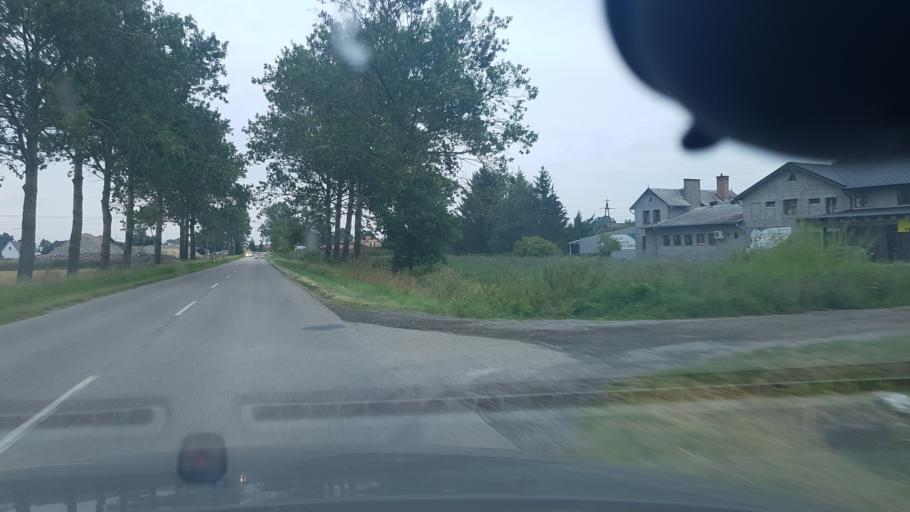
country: PL
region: Pomeranian Voivodeship
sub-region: Powiat nowodworski
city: Nowy Dwor Gdanski
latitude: 54.2180
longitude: 19.1096
